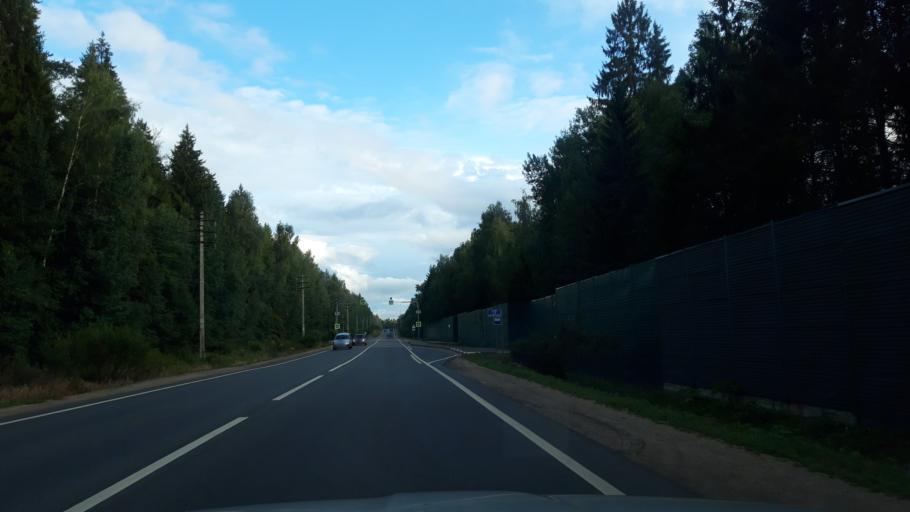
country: RU
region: Moskovskaya
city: Istra
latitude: 56.0628
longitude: 36.8965
